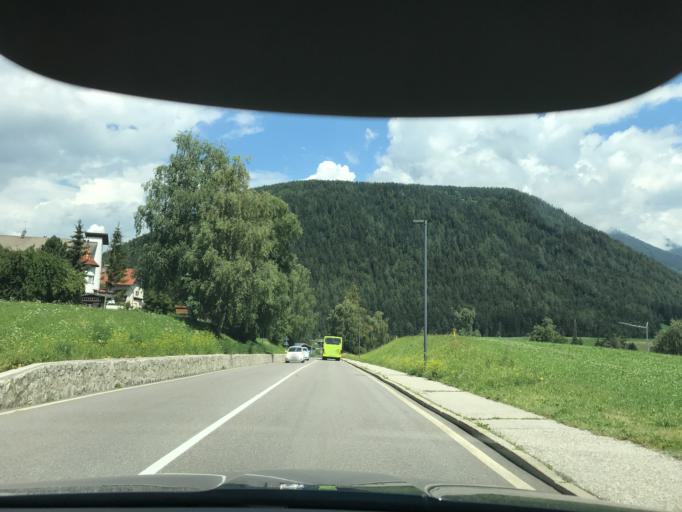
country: IT
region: Trentino-Alto Adige
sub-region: Bolzano
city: Valdaora di Mezzo
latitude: 46.7677
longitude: 12.0311
